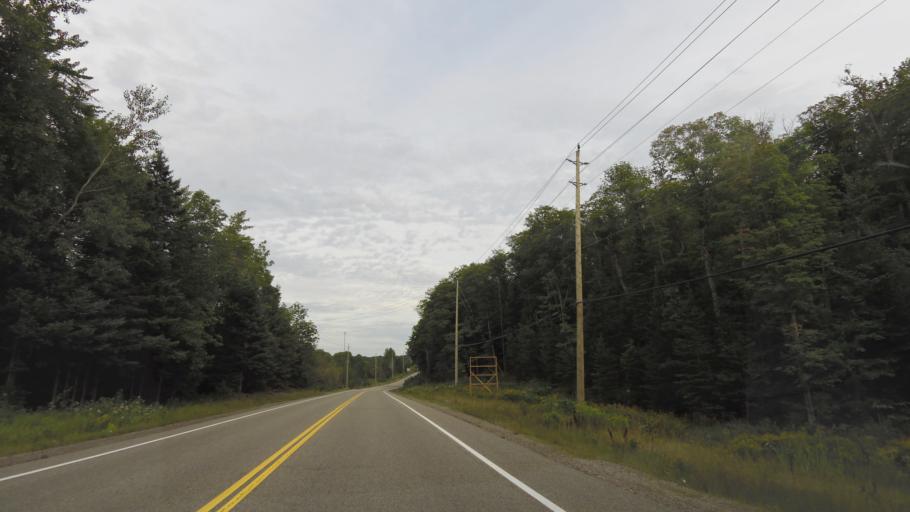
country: CA
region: Ontario
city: Bancroft
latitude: 45.0389
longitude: -78.4690
